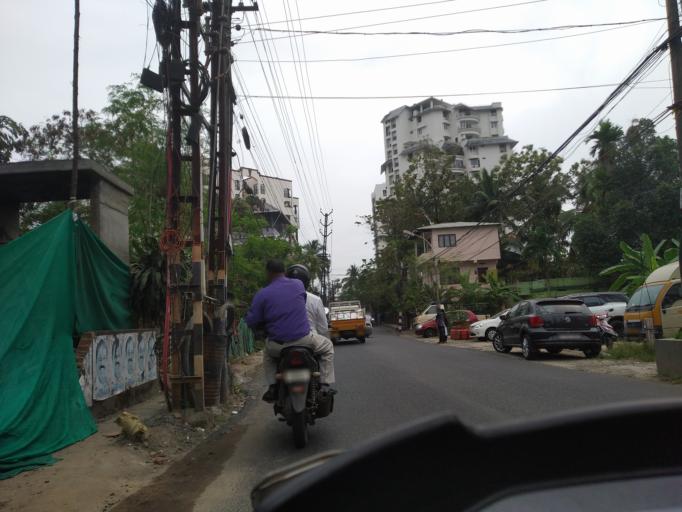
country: IN
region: Kerala
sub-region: Ernakulam
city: Cochin
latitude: 9.9361
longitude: 76.2975
